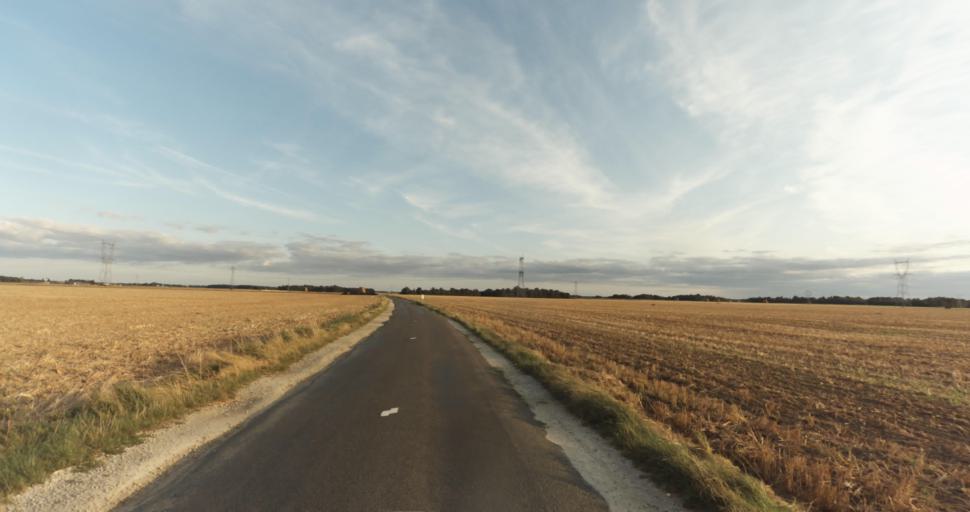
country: FR
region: Haute-Normandie
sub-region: Departement de l'Eure
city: Saint-Germain-sur-Avre
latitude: 48.8592
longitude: 1.2549
